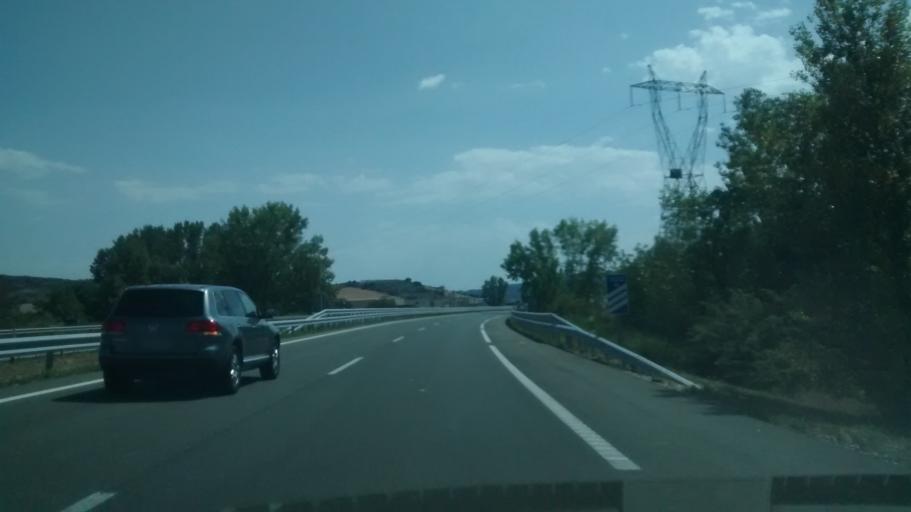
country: ES
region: Basque Country
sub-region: Provincia de Alava
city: Zambrana
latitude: 42.6830
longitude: -2.8901
